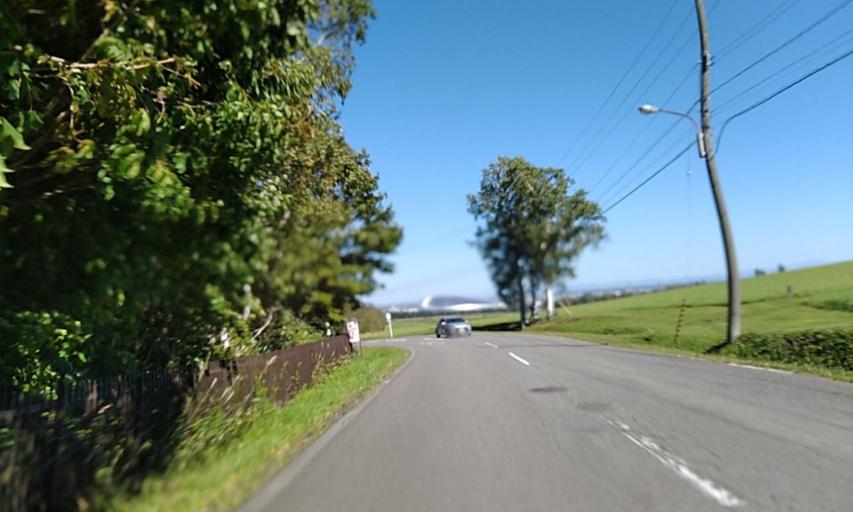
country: JP
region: Hokkaido
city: Sapporo
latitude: 43.0019
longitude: 141.3932
